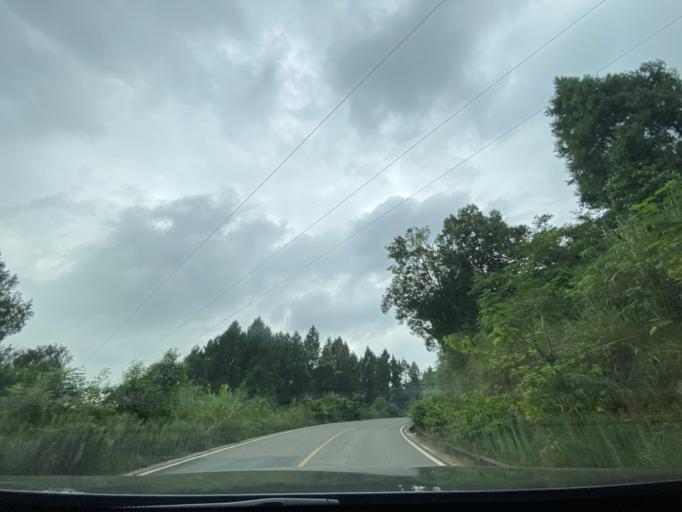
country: CN
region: Sichuan
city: Jiancheng
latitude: 30.5358
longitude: 104.5305
